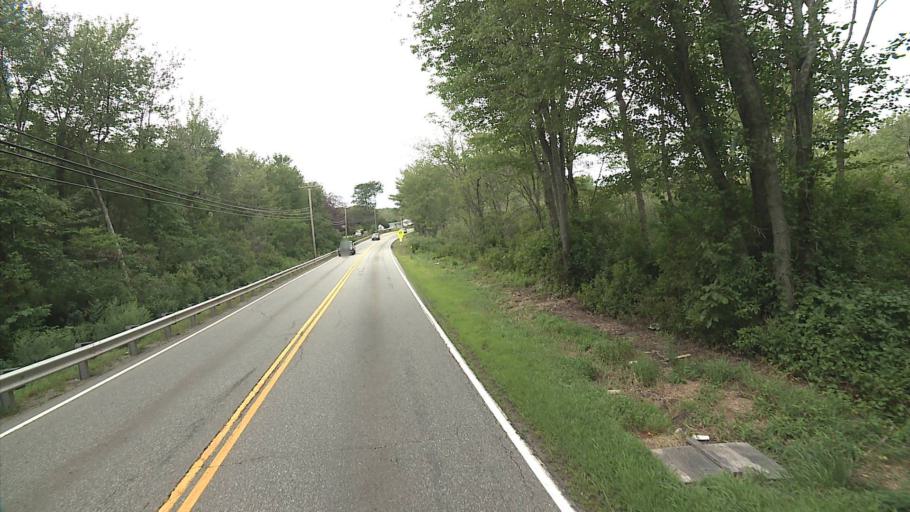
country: US
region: Connecticut
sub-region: New London County
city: Oxoboxo River
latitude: 41.4017
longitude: -72.1784
